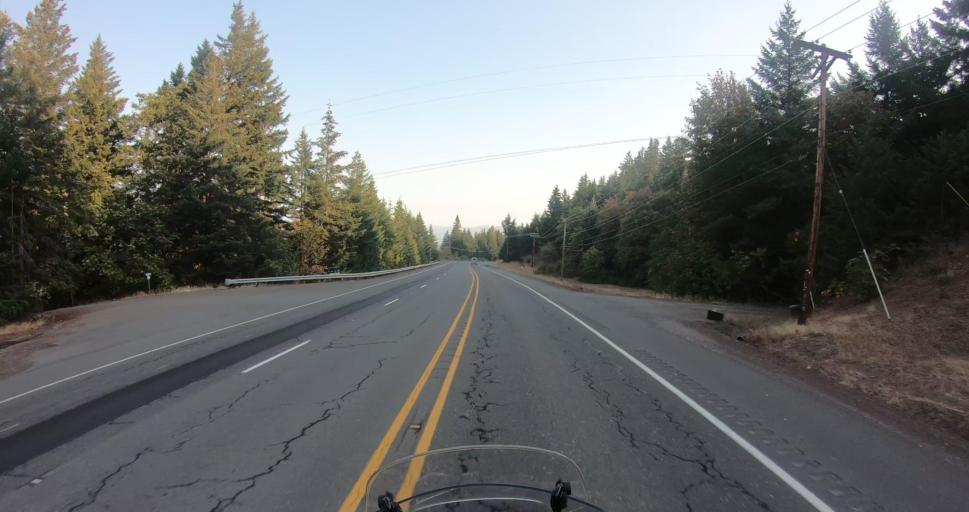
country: US
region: Oregon
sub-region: Hood River County
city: Odell
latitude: 45.5980
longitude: -121.5483
